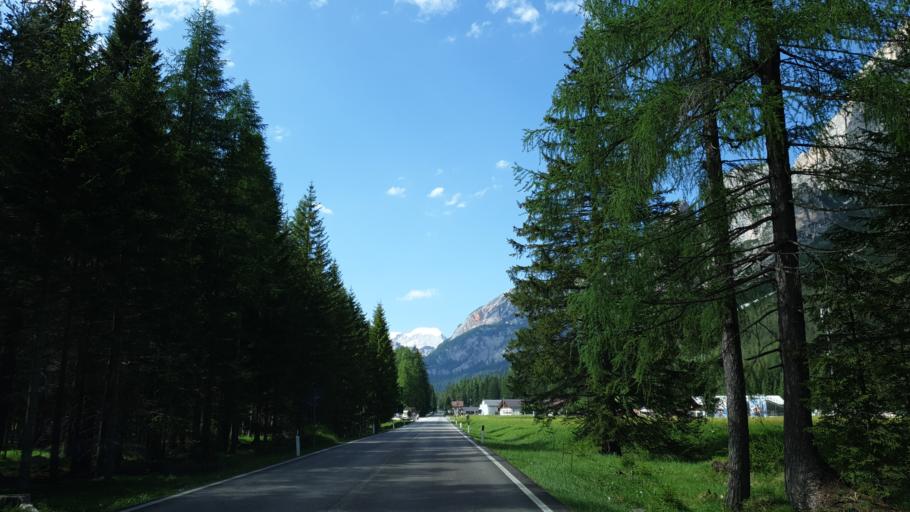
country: IT
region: Veneto
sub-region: Provincia di Belluno
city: Cortina d'Ampezzo
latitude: 46.5701
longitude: 12.1185
